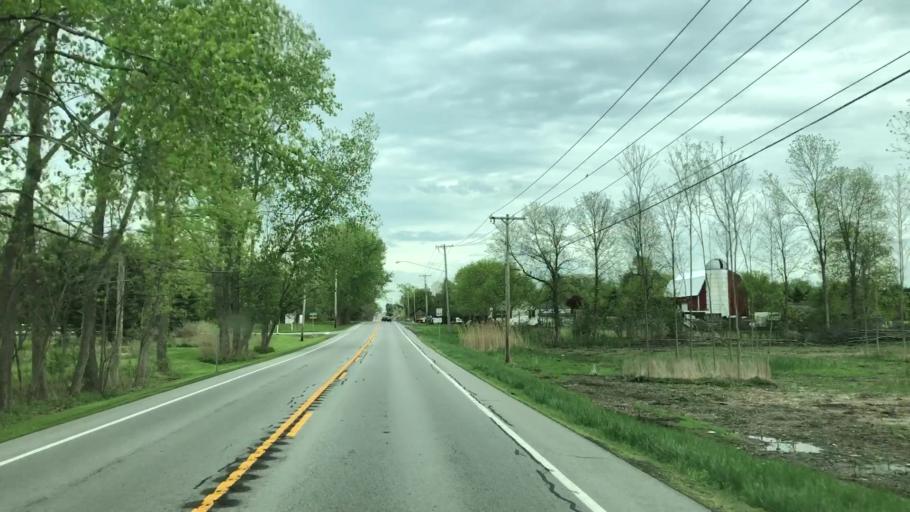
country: US
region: New York
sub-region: Monroe County
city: Fairport
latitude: 43.1307
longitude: -77.3886
